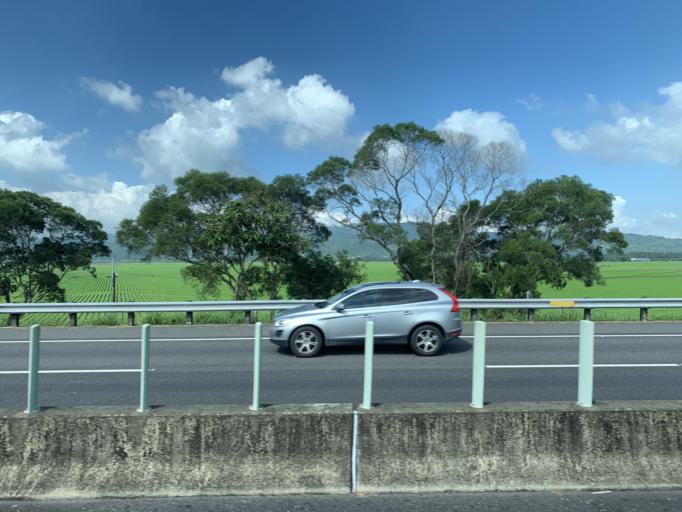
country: TW
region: Taiwan
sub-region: Pingtung
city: Pingtung
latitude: 22.8240
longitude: 120.4878
